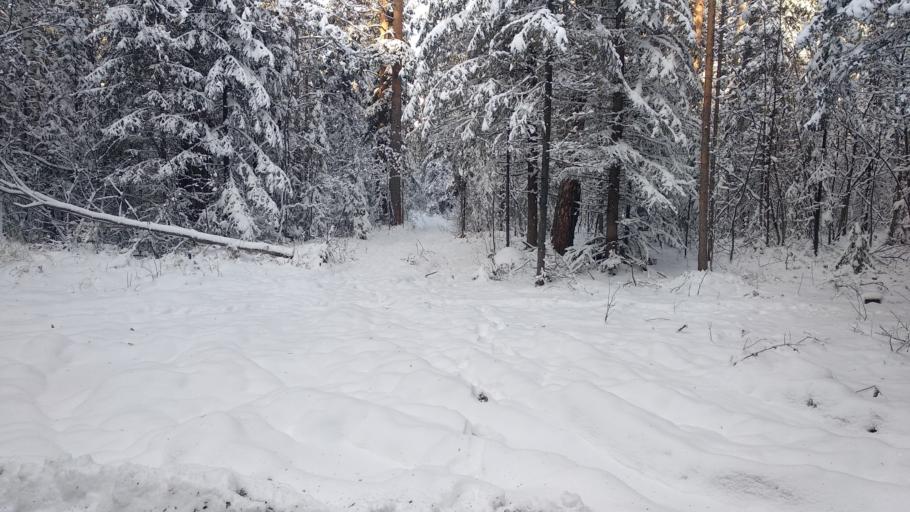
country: RU
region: Sverdlovsk
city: Krasnotur'insk
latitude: 59.7283
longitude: 60.1483
